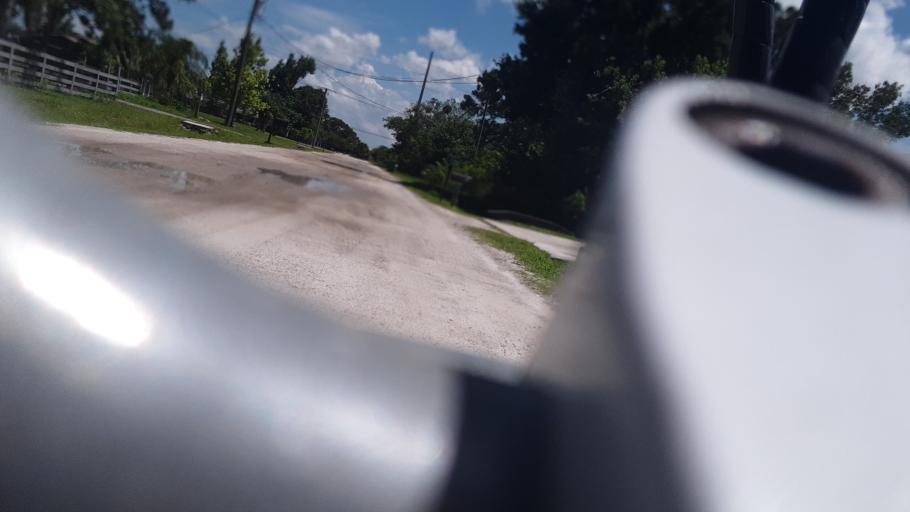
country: US
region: Florida
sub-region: Brevard County
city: Malabar
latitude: 27.9925
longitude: -80.6120
